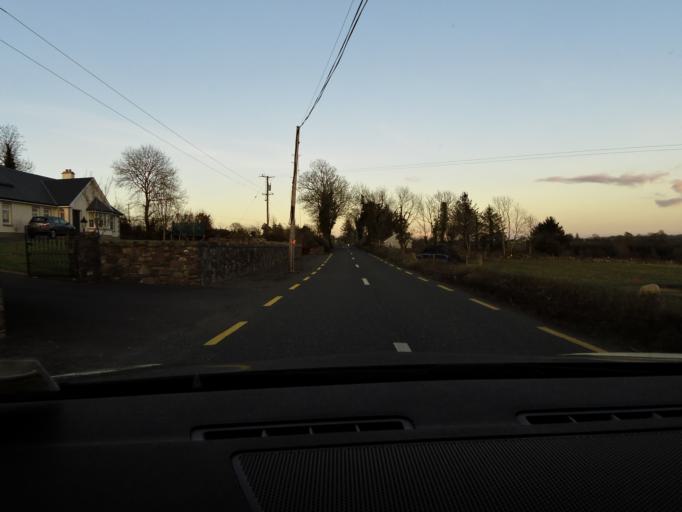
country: IE
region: Connaught
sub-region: Roscommon
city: Boyle
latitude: 53.9707
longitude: -8.3940
